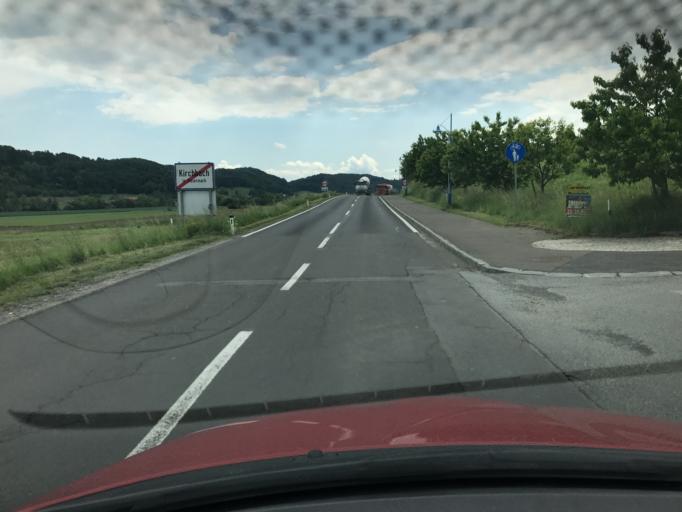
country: AT
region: Styria
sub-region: Politischer Bezirk Suedoststeiermark
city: Kirchbach in Steiermark
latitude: 46.9263
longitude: 15.6671
